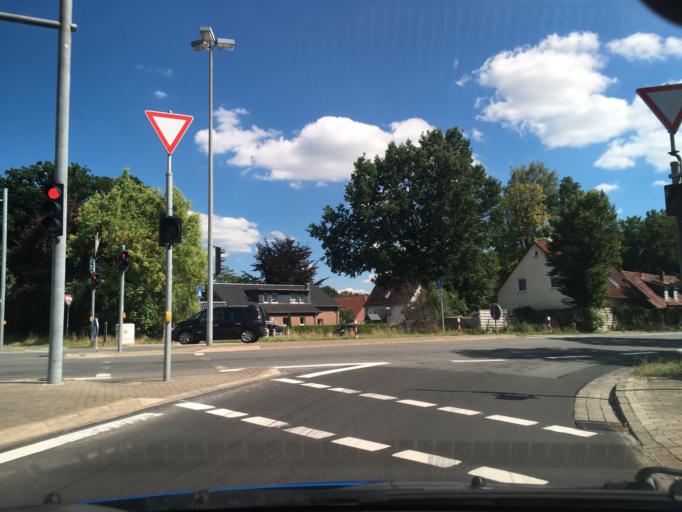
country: DE
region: Lower Saxony
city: Celle
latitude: 52.6226
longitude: 10.1296
